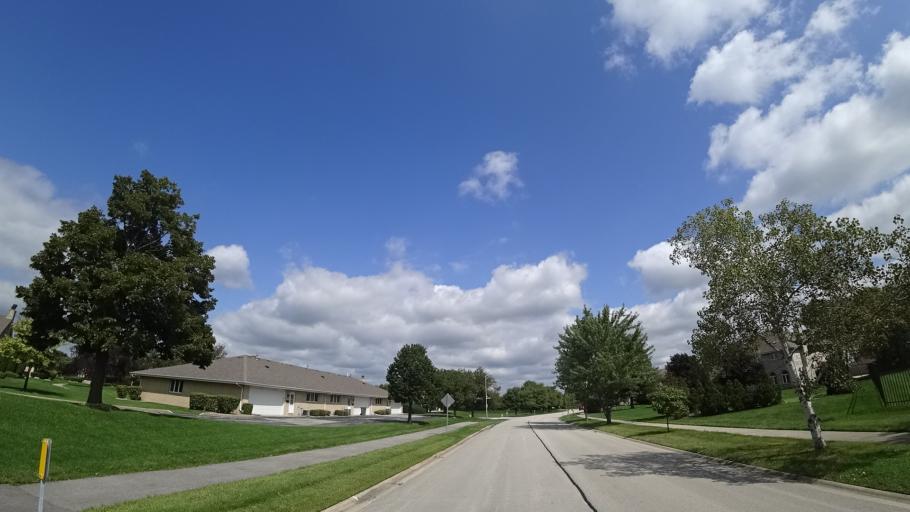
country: US
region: Illinois
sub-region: Will County
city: Mokena
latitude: 41.5620
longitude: -87.8814
